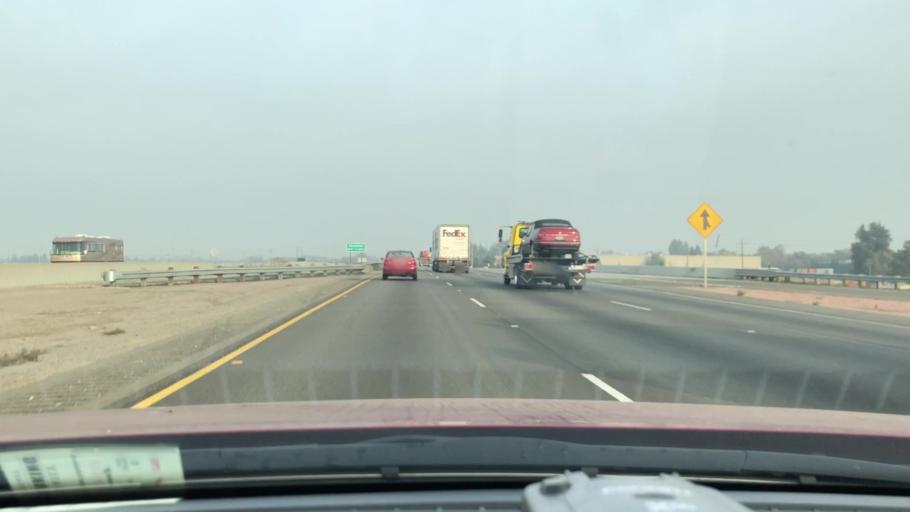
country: US
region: California
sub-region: San Joaquin County
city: French Camp
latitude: 37.8962
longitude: -121.2835
